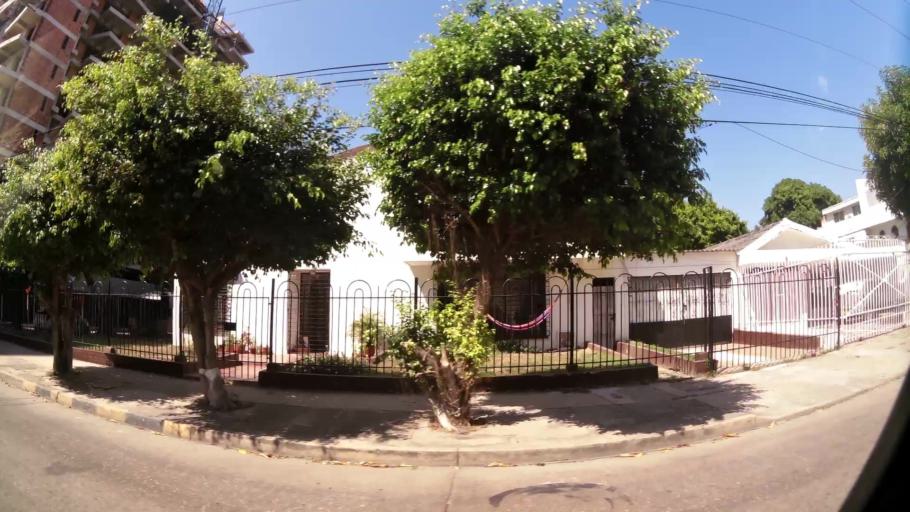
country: CO
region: Bolivar
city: Cartagena
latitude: 10.4450
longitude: -75.5196
